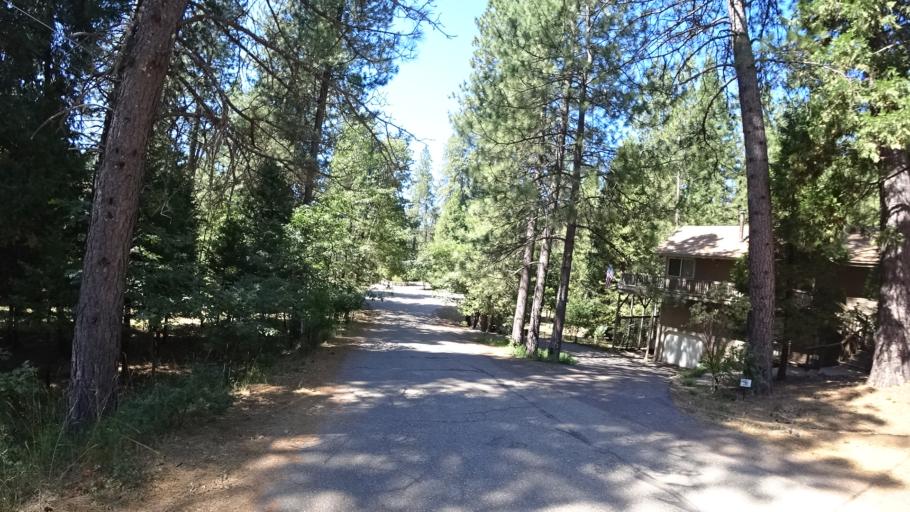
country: US
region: California
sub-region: Calaveras County
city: Arnold
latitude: 38.2358
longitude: -120.3751
